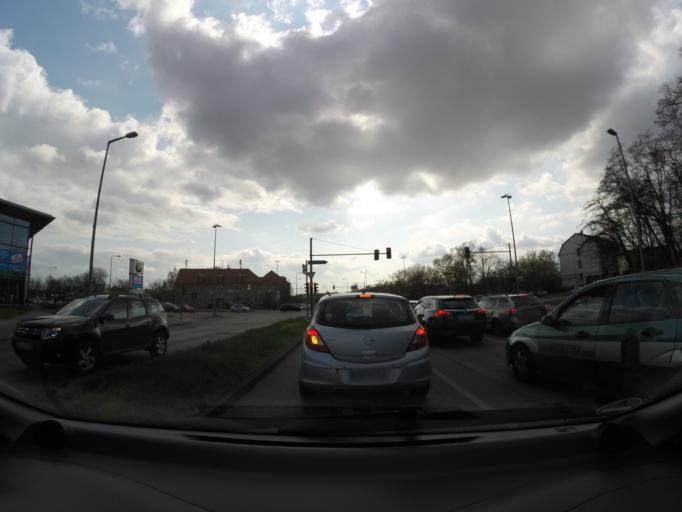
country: DE
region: Berlin
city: Hellersdorf
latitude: 52.5257
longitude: 13.6088
